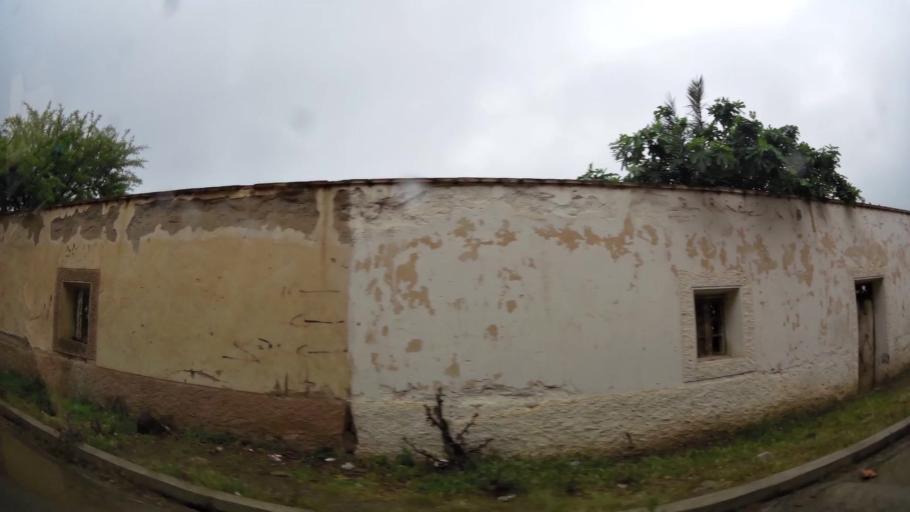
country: MA
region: Oriental
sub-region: Nador
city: Nador
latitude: 35.1549
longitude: -2.9607
